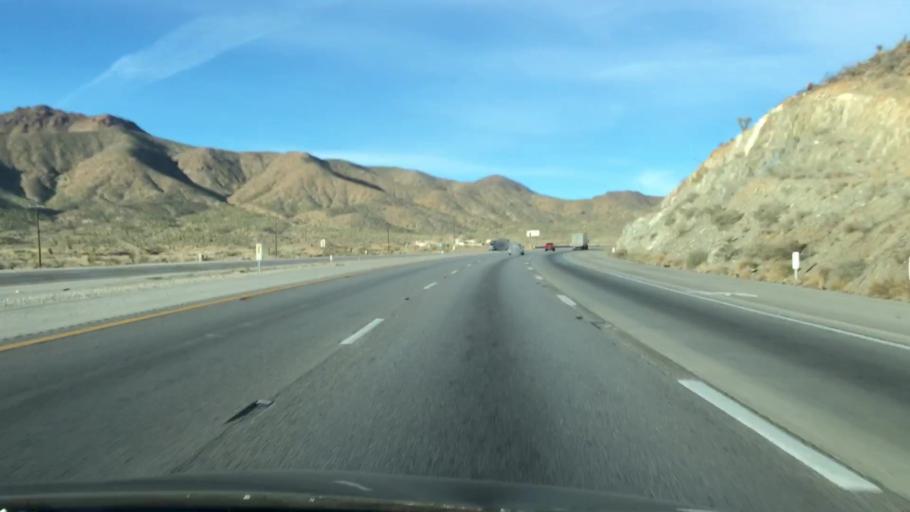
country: US
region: Nevada
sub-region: Clark County
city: Sandy Valley
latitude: 35.4614
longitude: -115.4694
